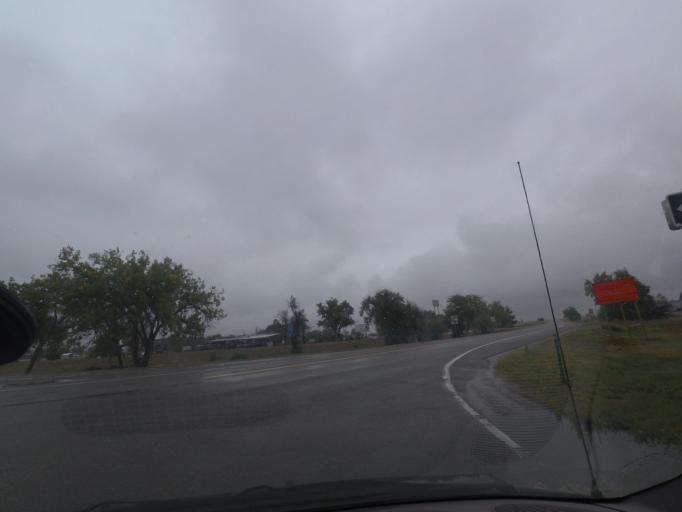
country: US
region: Colorado
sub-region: Arapahoe County
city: Byers
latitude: 39.7163
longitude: -104.2212
